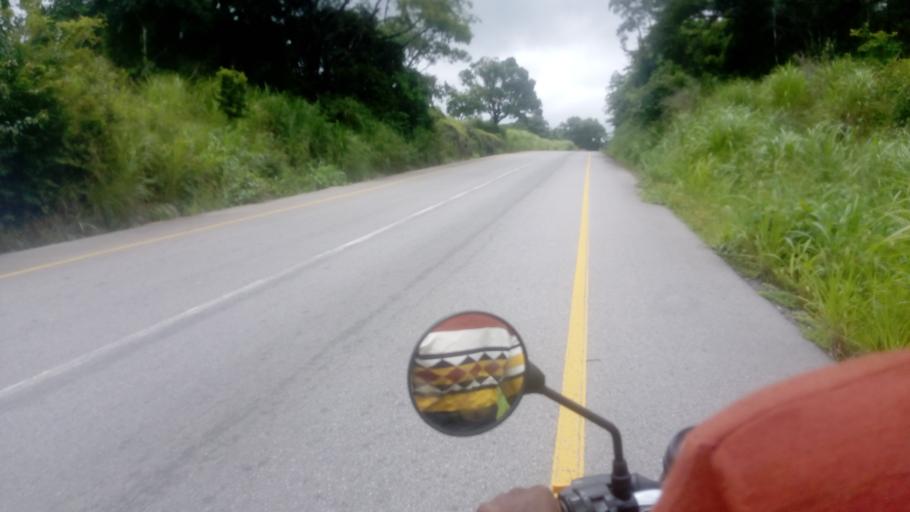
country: SL
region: Northern Province
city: Masaka
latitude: 8.6511
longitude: -11.7755
